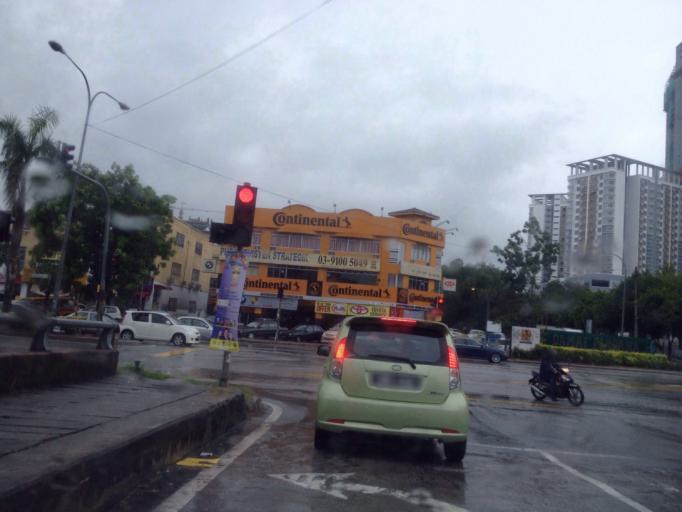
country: MY
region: Selangor
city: Kampong Baharu Balakong
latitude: 3.0547
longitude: 101.7445
